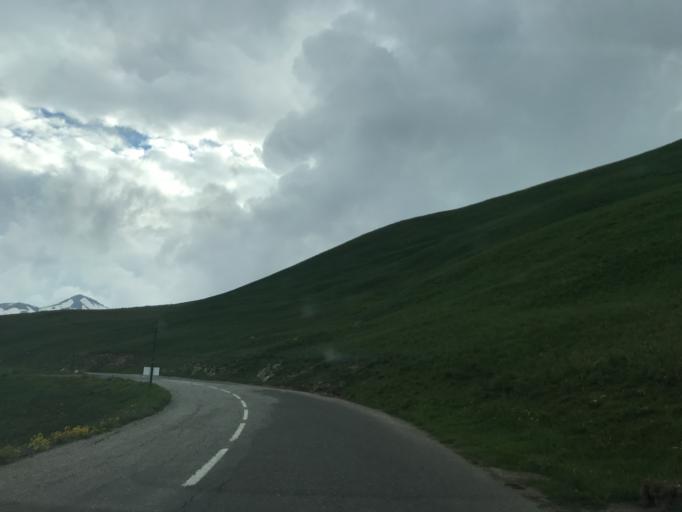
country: FR
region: Rhone-Alpes
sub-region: Departement de la Savoie
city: Valloire
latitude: 45.0792
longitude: 6.4154
